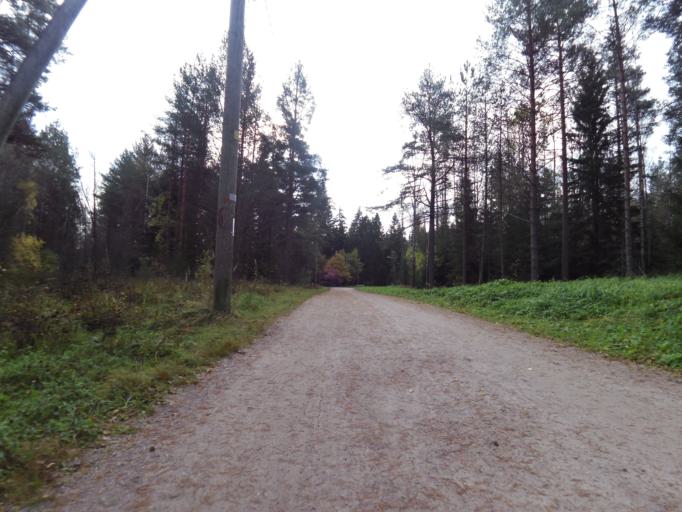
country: FI
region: Uusimaa
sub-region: Helsinki
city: Kauniainen
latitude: 60.1812
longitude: 24.6995
